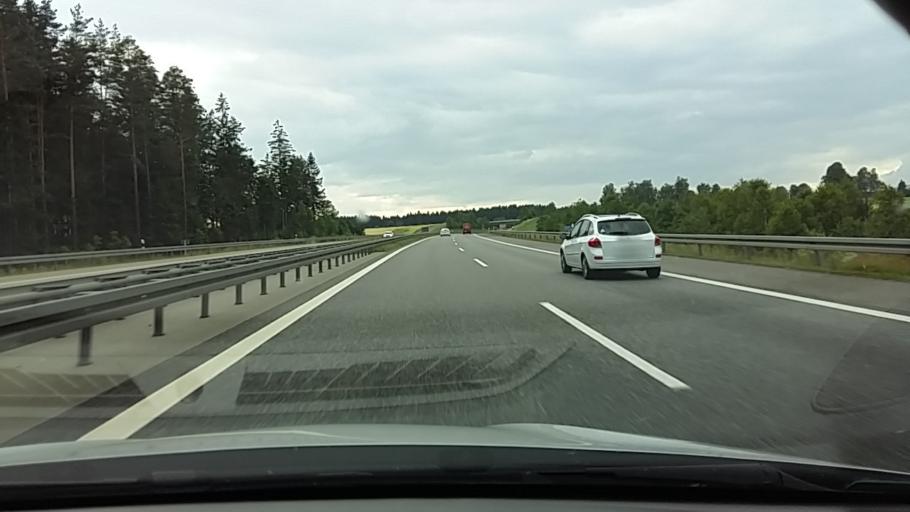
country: DE
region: Bavaria
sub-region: Upper Palatinate
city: Moosbach
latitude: 49.6115
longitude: 12.3872
